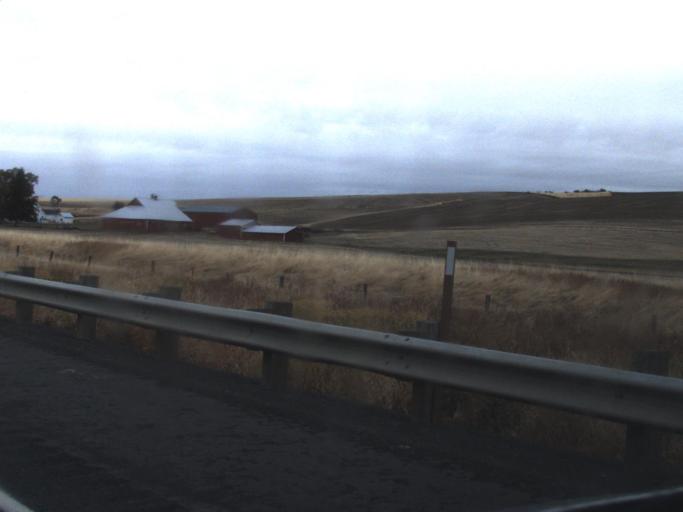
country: US
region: Washington
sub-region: Asotin County
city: Clarkston
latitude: 46.5658
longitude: -117.1154
